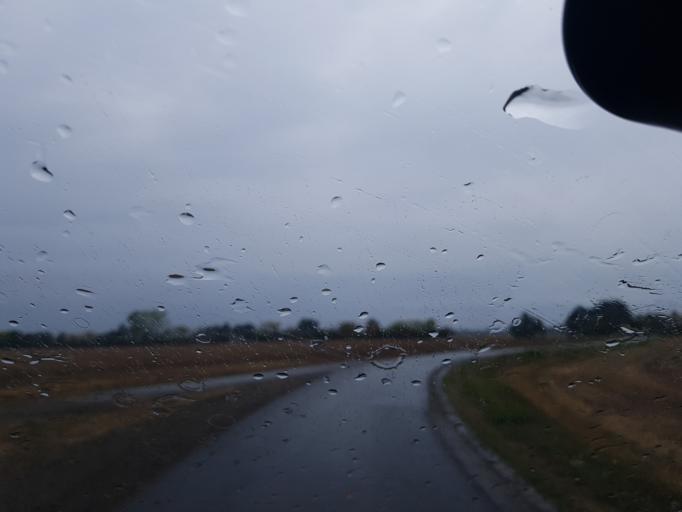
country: DE
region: Saxony-Anhalt
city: Jessen
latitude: 51.7766
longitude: 12.8875
